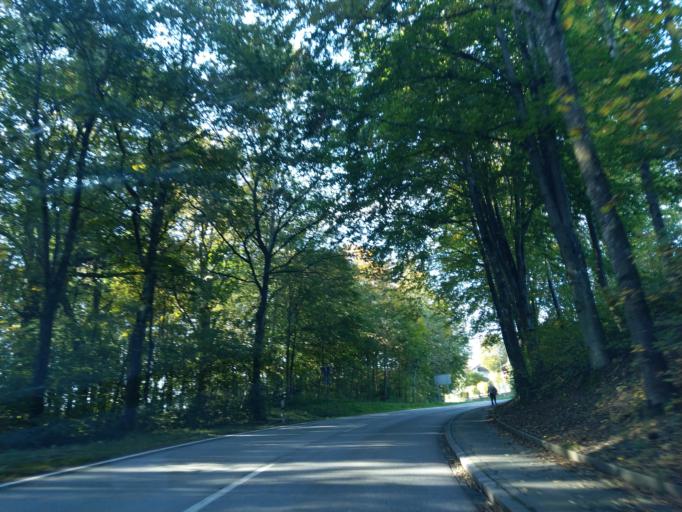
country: DE
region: Bavaria
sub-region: Lower Bavaria
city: Metten
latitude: 48.8834
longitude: 12.9227
